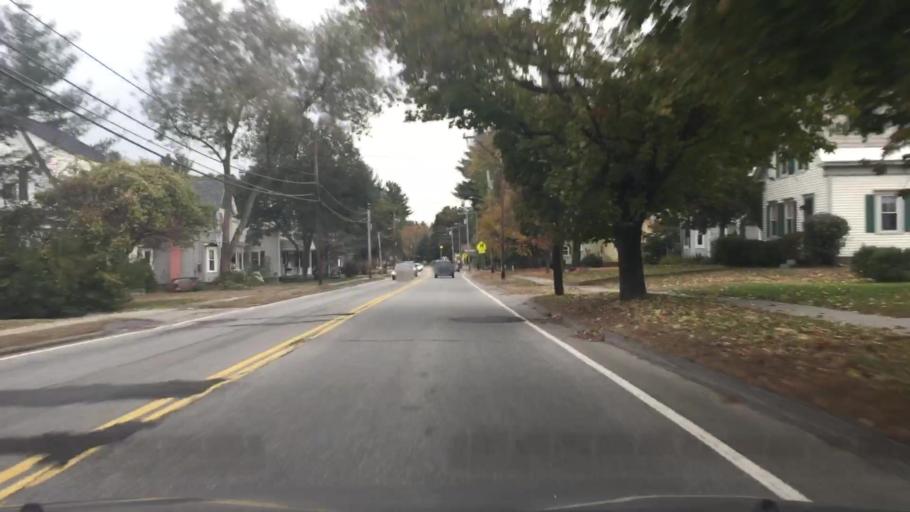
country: US
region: New Hampshire
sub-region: Cheshire County
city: Keene
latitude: 42.9373
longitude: -72.3036
